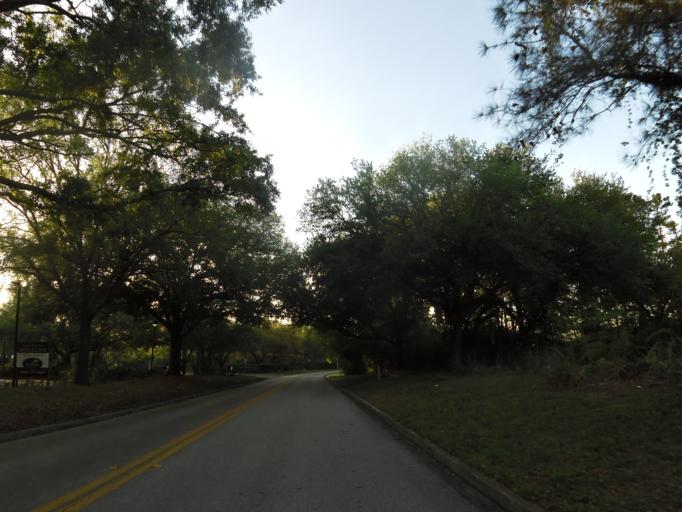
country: US
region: Florida
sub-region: Duval County
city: Jacksonville
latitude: 30.2555
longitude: -81.5901
